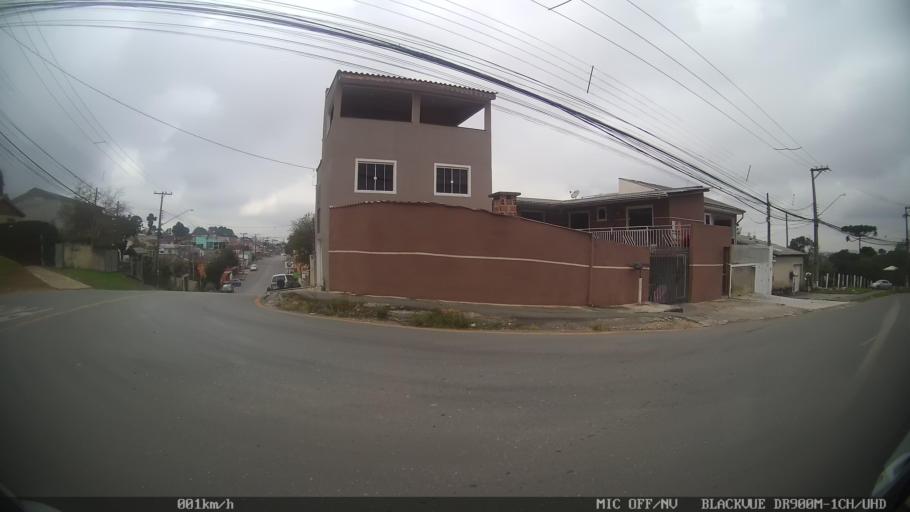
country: BR
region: Parana
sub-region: Almirante Tamandare
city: Almirante Tamandare
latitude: -25.3510
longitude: -49.2712
